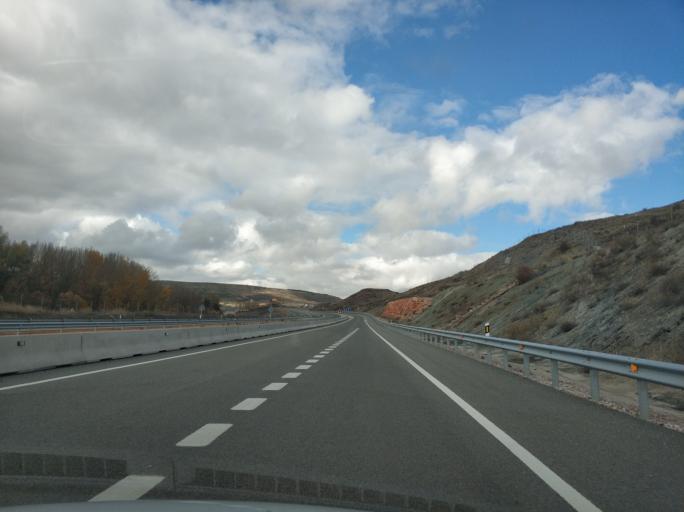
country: ES
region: Castille and Leon
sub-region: Provincia de Soria
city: Medinaceli
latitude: 41.1738
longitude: -2.4215
